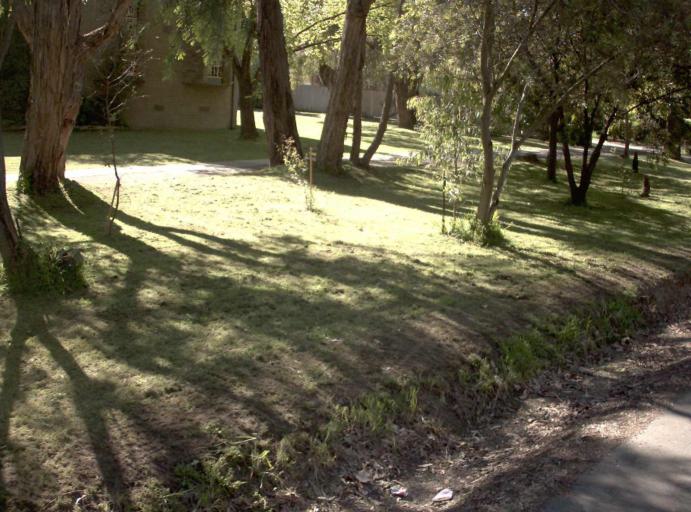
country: AU
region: Victoria
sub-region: Maroondah
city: Croydon North
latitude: -37.7920
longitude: 145.2820
